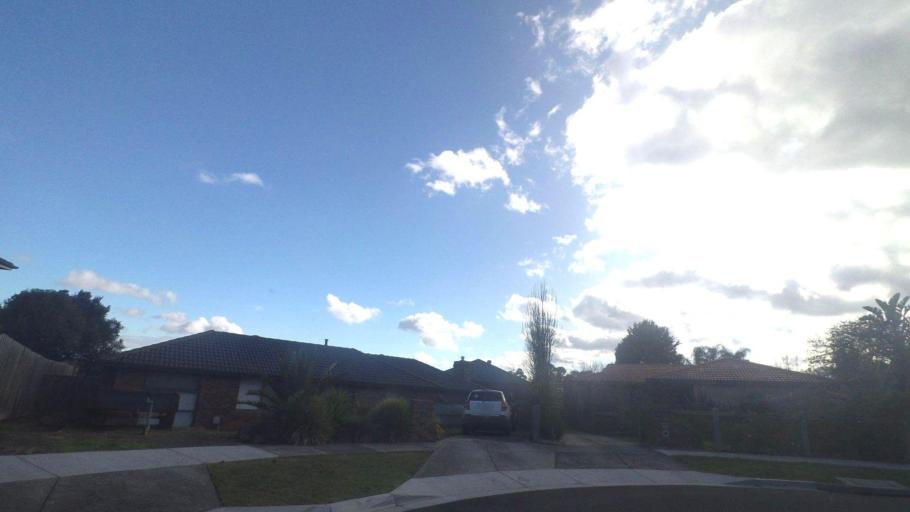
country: AU
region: Victoria
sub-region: Knox
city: Scoresby
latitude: -37.9131
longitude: 145.2440
